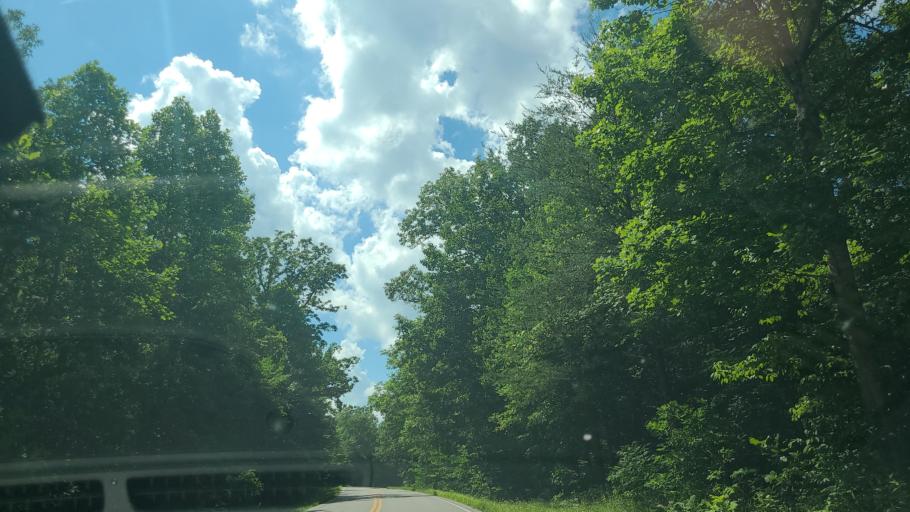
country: US
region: Kentucky
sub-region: Whitley County
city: Williamsburg
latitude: 36.8393
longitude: -84.2744
